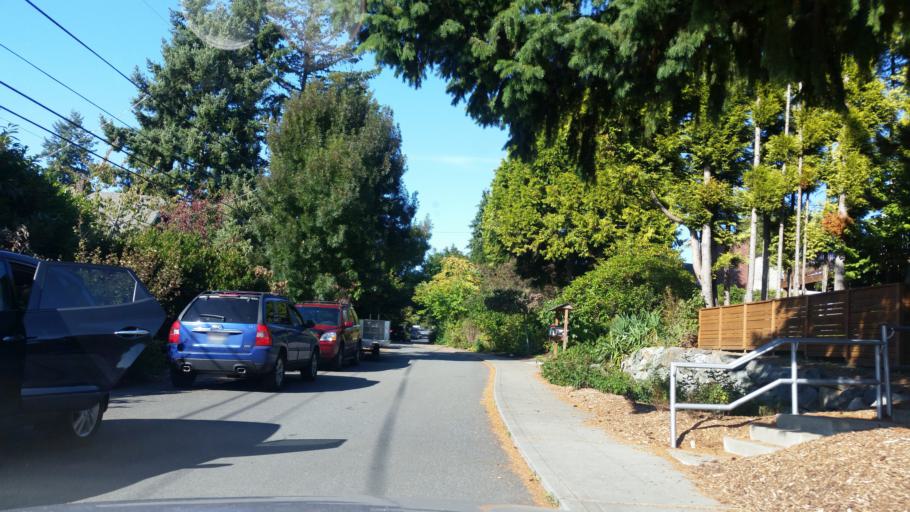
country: US
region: Washington
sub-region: King County
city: Shoreline
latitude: 47.7070
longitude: -122.3595
